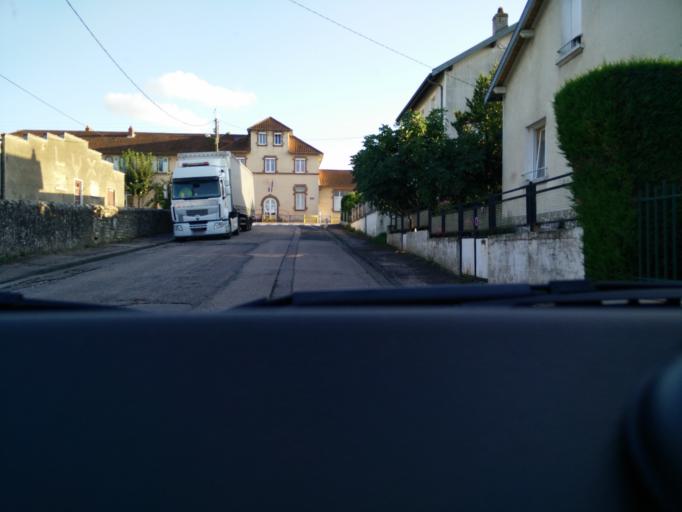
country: FR
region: Lorraine
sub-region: Departement de Meurthe-et-Moselle
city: Damelevieres
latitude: 48.5547
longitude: 6.4054
